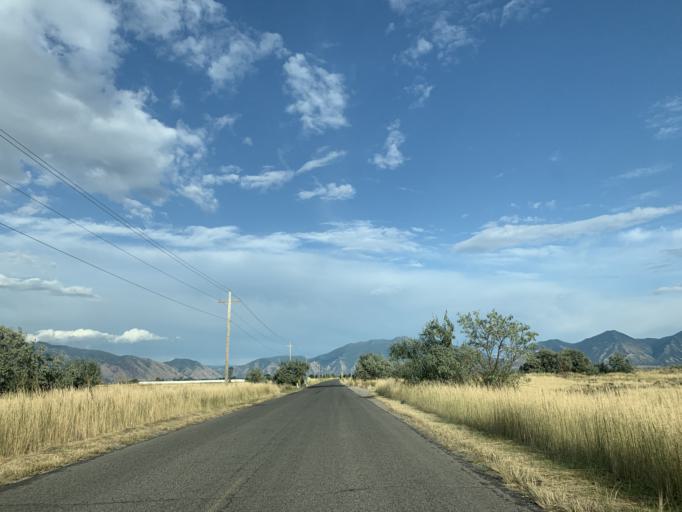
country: US
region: Utah
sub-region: Utah County
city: West Mountain
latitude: 40.1142
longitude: -111.7943
